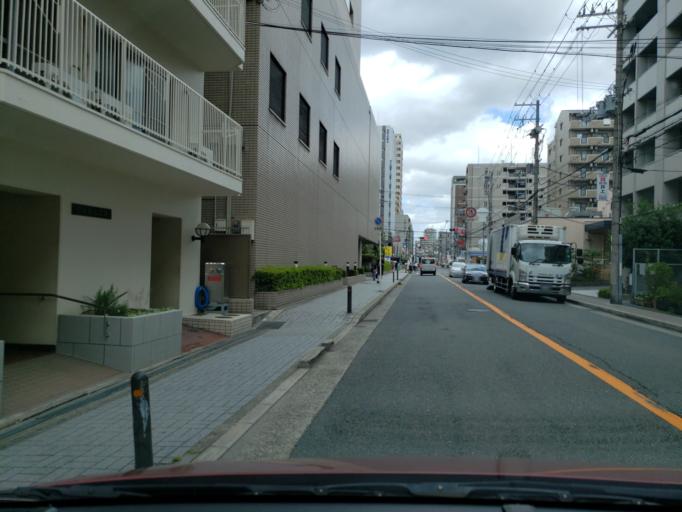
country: JP
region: Osaka
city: Suita
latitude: 34.7613
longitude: 135.4983
